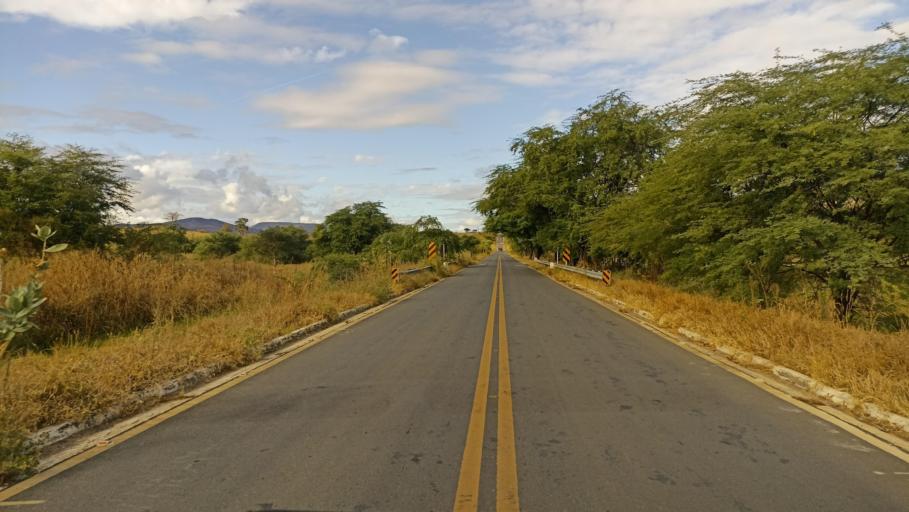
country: BR
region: Minas Gerais
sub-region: Itinga
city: Itinga
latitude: -16.5829
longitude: -41.6437
